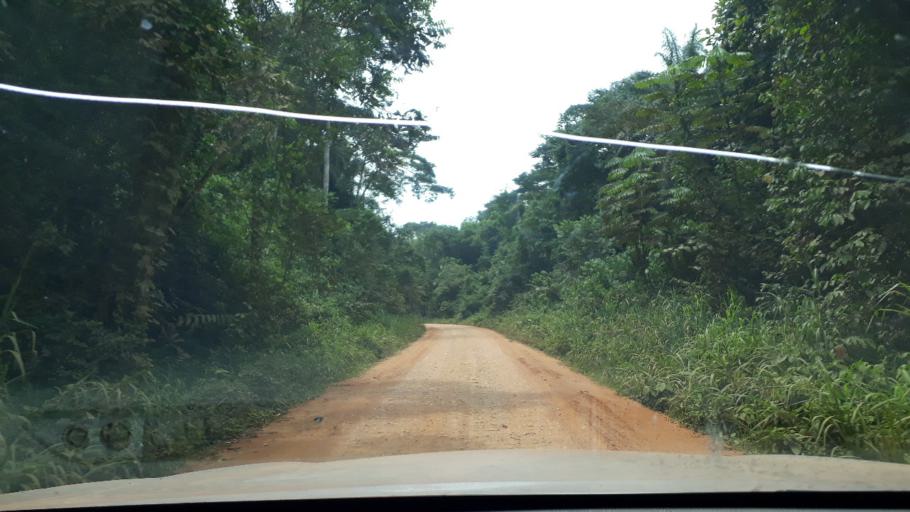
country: CD
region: Eastern Province
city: Wamba
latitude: 1.4125
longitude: 28.4510
